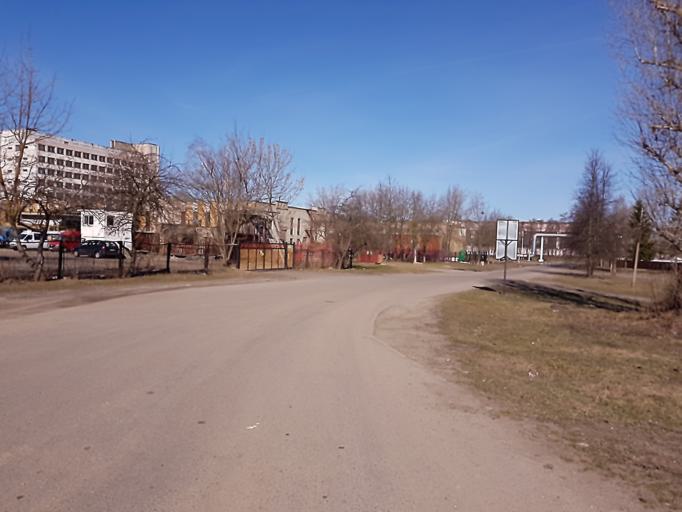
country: BY
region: Mogilev
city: Babruysk
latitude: 53.1795
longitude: 29.2085
